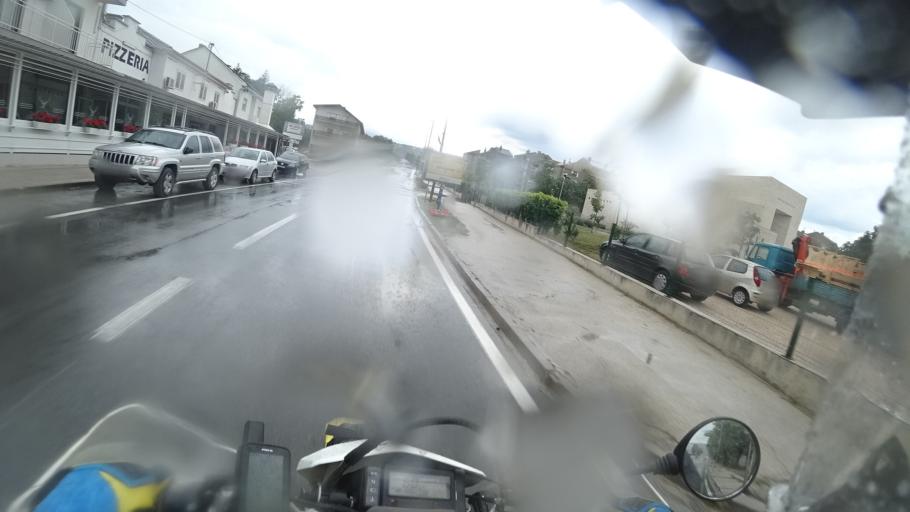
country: HR
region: Sibensko-Kniniska
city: Knin
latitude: 44.0408
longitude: 16.2008
